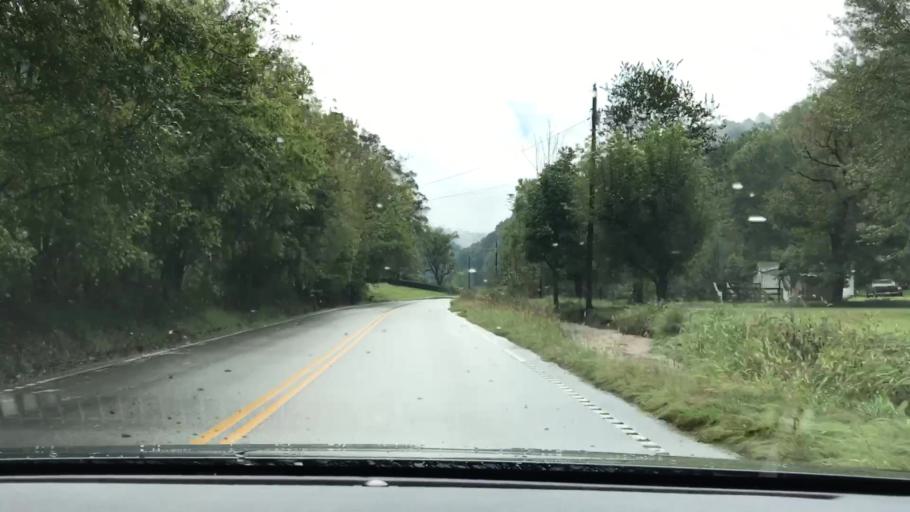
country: US
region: Tennessee
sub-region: Macon County
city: Red Boiling Springs
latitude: 36.4165
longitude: -85.9283
